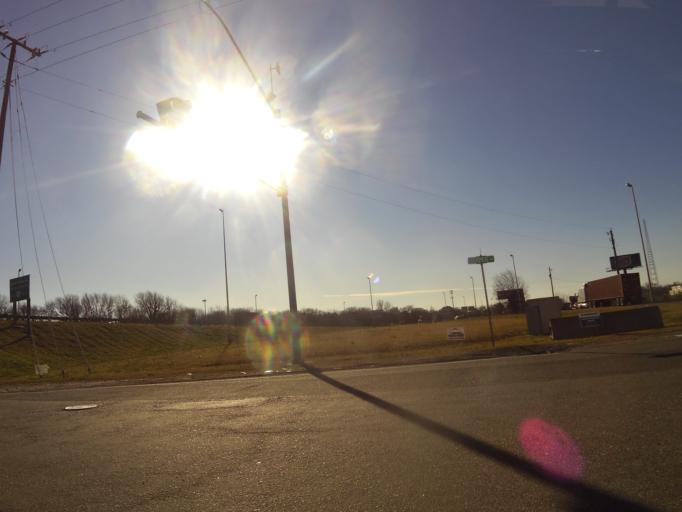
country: US
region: Virginia
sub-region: City of Portsmouth
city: Portsmouth
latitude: 36.8450
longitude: -76.3303
